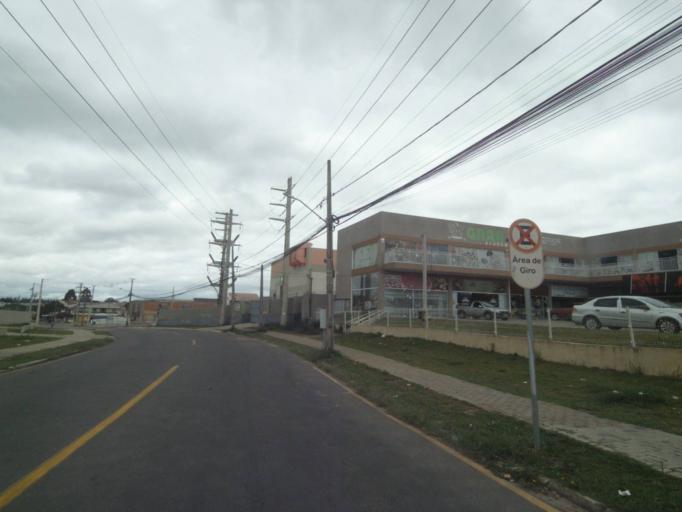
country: BR
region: Parana
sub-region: Sao Jose Dos Pinhais
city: Sao Jose dos Pinhais
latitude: -25.5574
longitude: -49.2548
